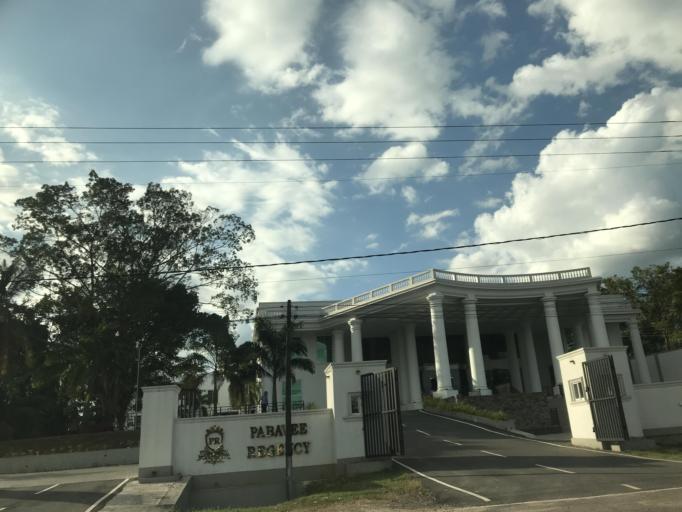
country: LK
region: Western
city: Gampaha
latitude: 7.0592
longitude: 80.0091
